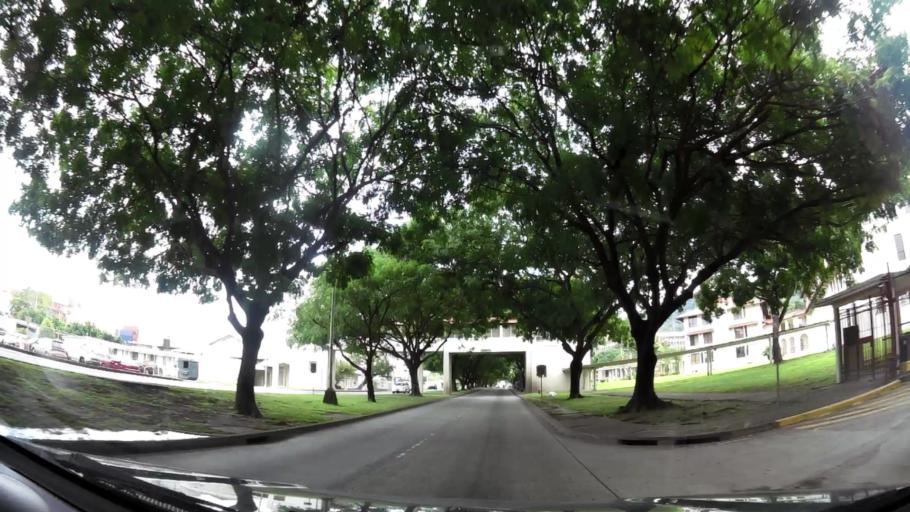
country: PA
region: Panama
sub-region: Distrito de Panama
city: Ancon
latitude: 8.9585
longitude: -79.5586
